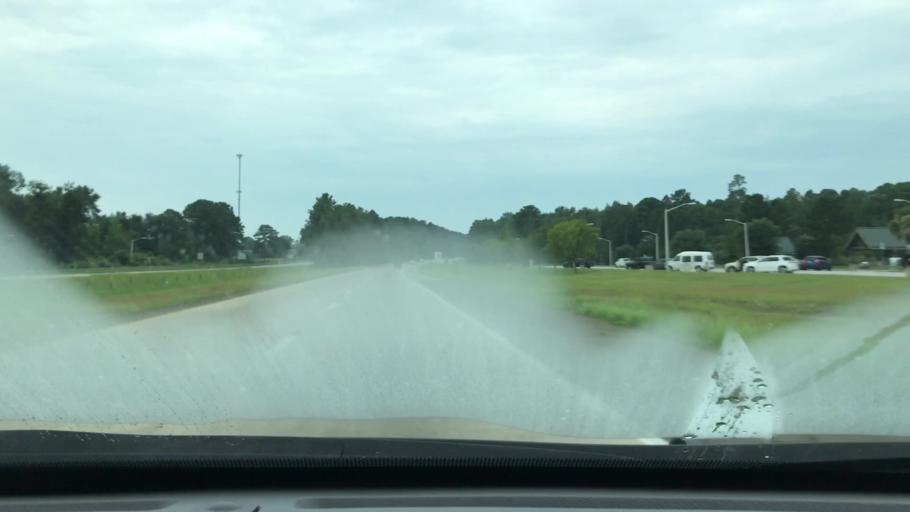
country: US
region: South Carolina
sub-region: Hampton County
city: Yemassee
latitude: 32.8002
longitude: -80.7721
